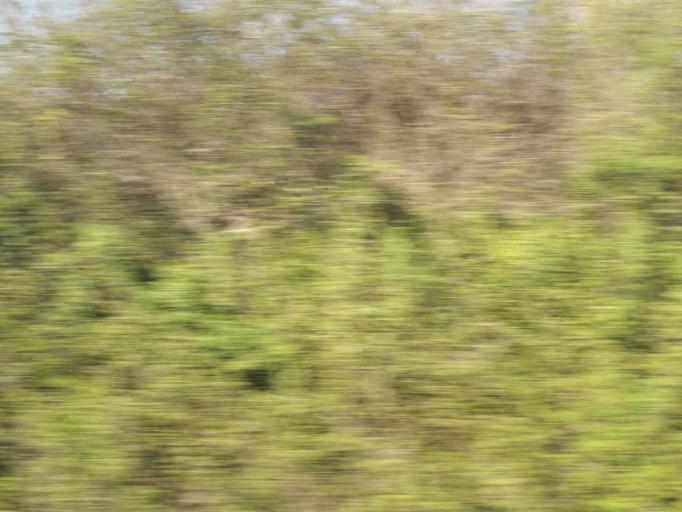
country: FR
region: Rhone-Alpes
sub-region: Departement de l'Isere
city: Saint-Lattier
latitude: 45.0860
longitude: 5.2034
